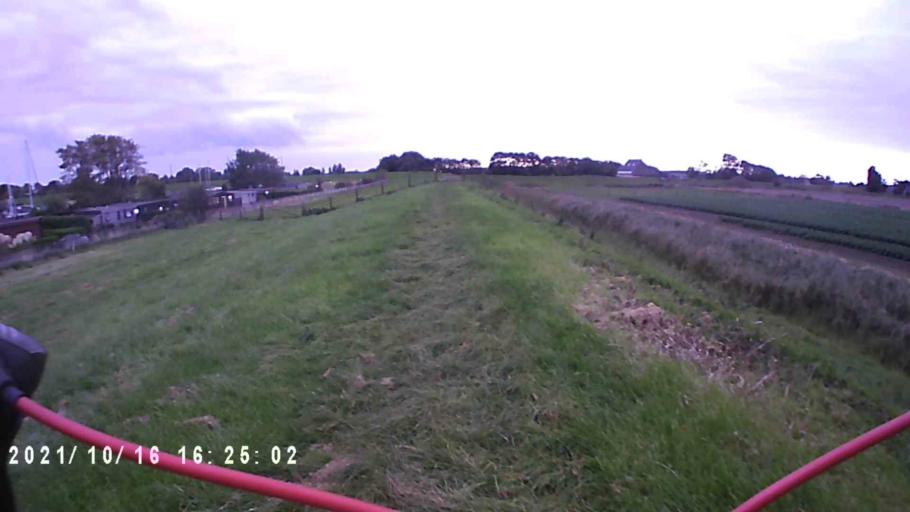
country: NL
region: Friesland
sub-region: Gemeente Dongeradeel
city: Anjum
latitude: 53.3839
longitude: 6.1559
